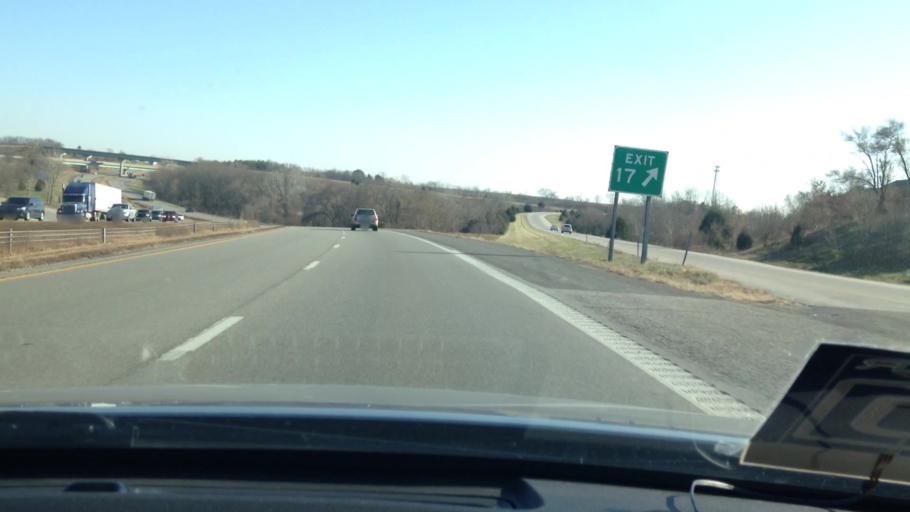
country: US
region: Missouri
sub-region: Platte County
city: Platte City
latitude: 39.3489
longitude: -94.7567
